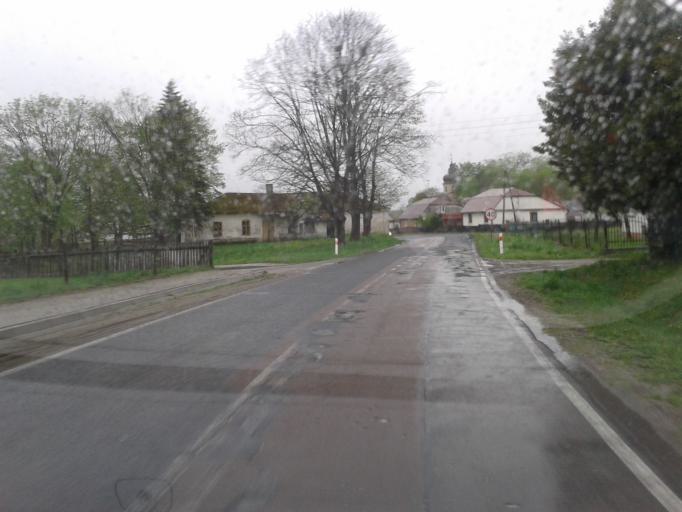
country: PL
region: Subcarpathian Voivodeship
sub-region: Powiat lubaczowski
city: Narol
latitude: 50.3141
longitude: 23.2451
